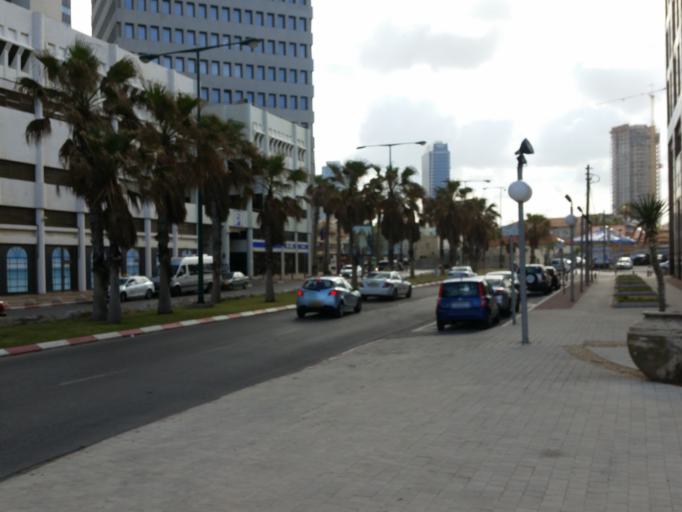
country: IL
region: Tel Aviv
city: Yafo
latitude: 32.0627
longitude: 34.7618
